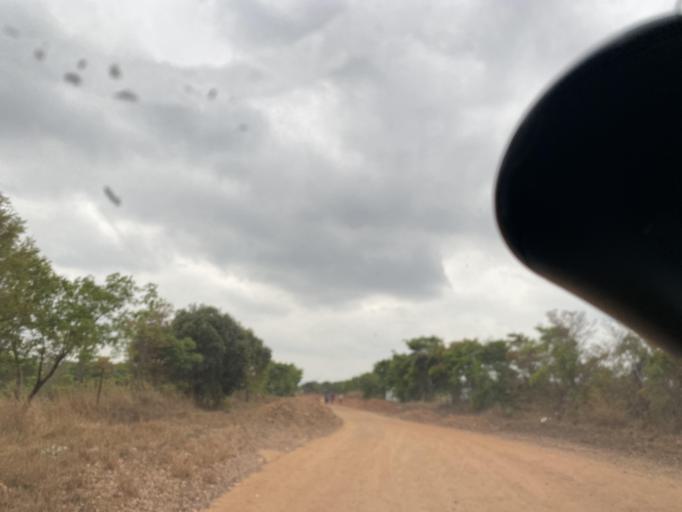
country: ZM
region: Lusaka
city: Chongwe
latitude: -15.2615
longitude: 28.7320
